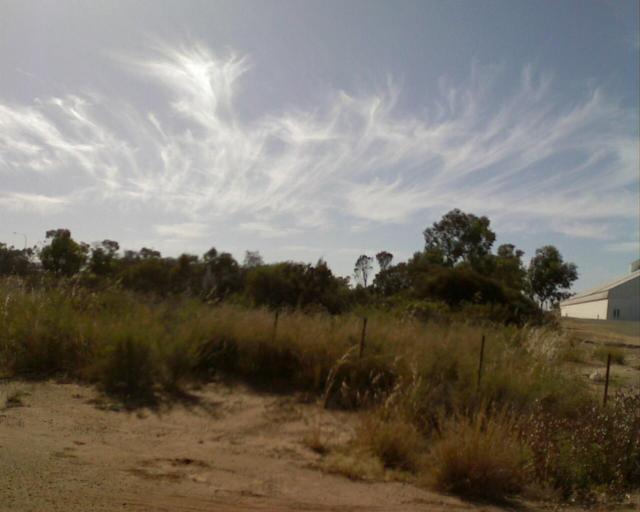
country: AU
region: Western Australia
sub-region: Wongan-Ballidu
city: Wongan Hills
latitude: -30.1054
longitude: 116.6283
